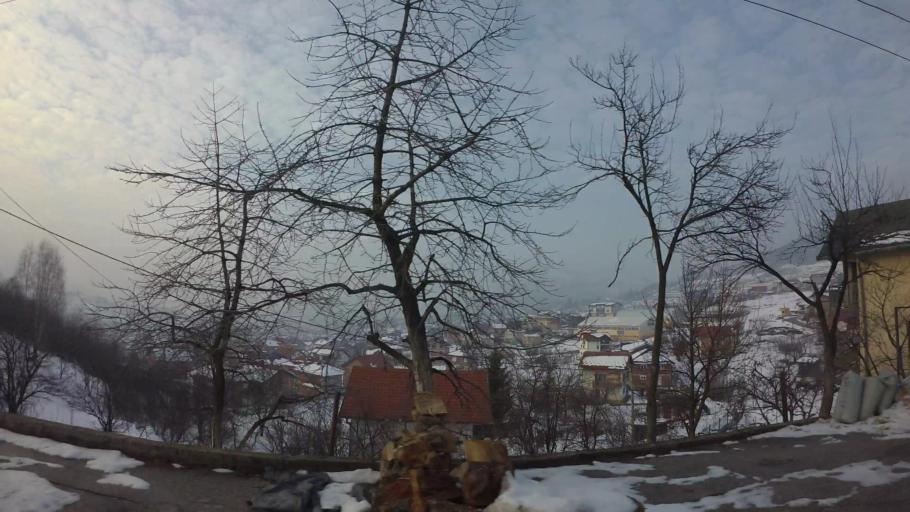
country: BA
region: Federation of Bosnia and Herzegovina
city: Hotonj
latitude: 43.8938
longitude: 18.3838
